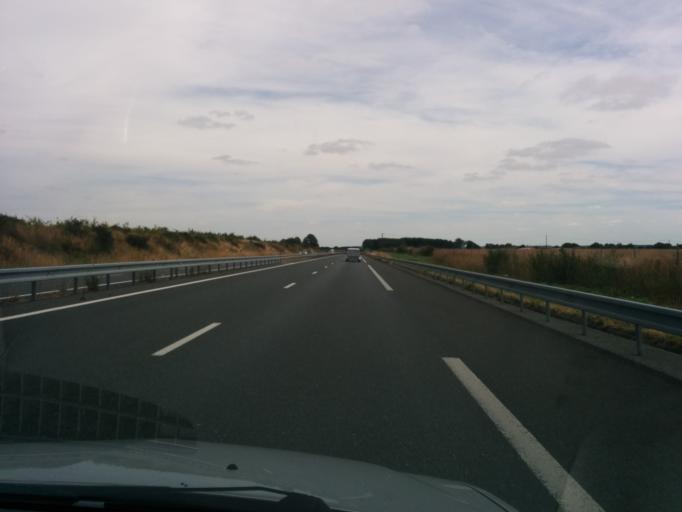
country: FR
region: Poitou-Charentes
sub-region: Departement des Deux-Sevres
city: Saint-Pierre-des-Echaubrognes
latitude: 46.9271
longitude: -0.7168
